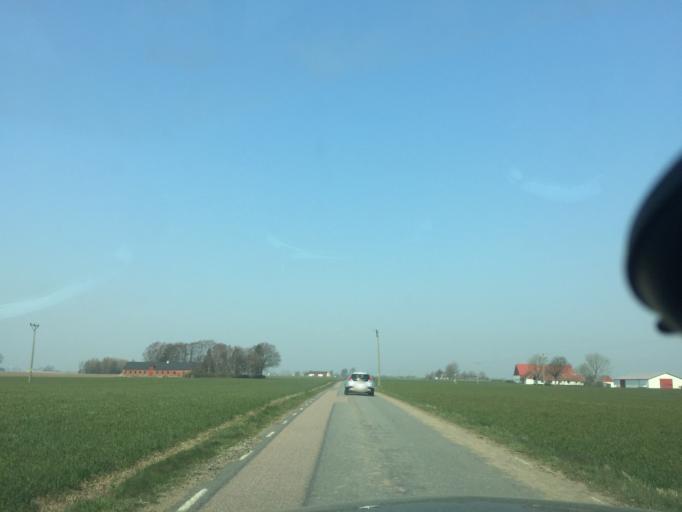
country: SE
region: Skane
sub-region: Simrishamns Kommun
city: Simrishamn
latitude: 55.4504
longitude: 14.2162
